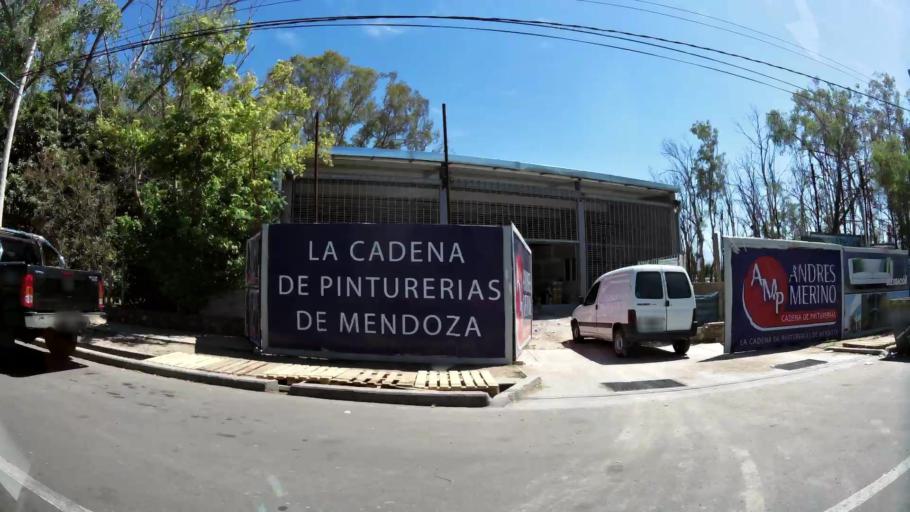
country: AR
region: Mendoza
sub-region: Departamento de Godoy Cruz
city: Godoy Cruz
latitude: -32.9533
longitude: -68.8561
